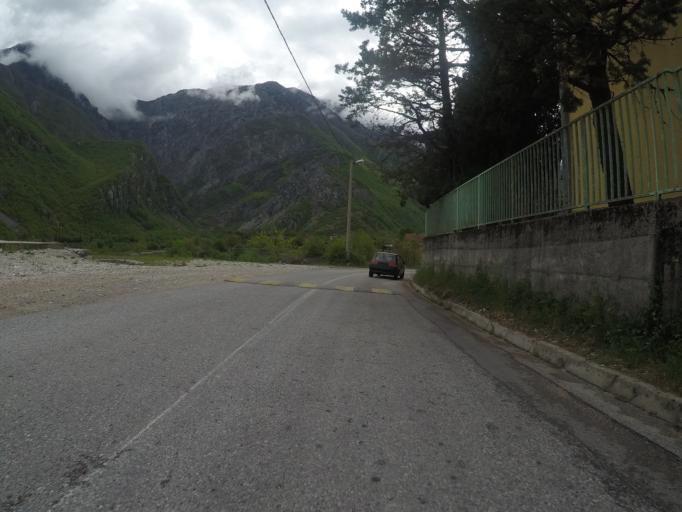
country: BA
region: Federation of Bosnia and Herzegovina
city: Siroki Brijeg
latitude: 43.5419
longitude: 17.5666
